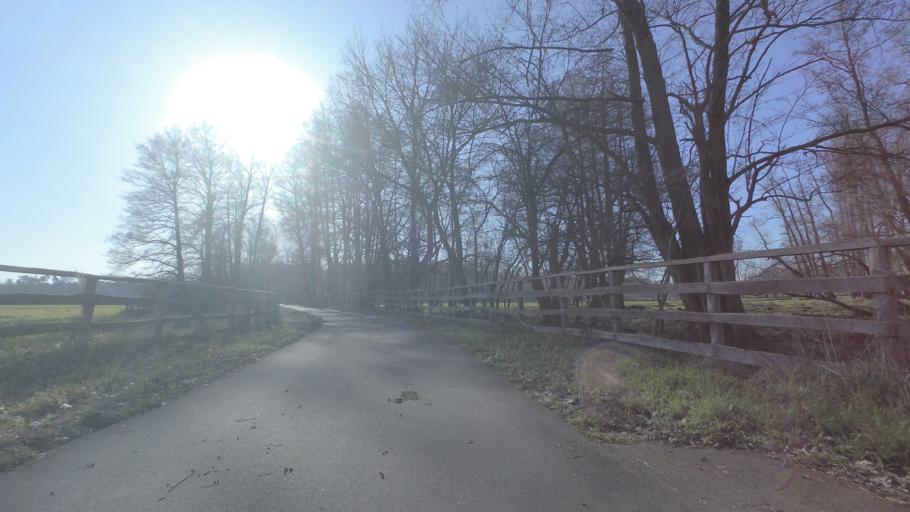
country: DE
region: Brandenburg
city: Luckenwalde
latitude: 52.0660
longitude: 13.1661
